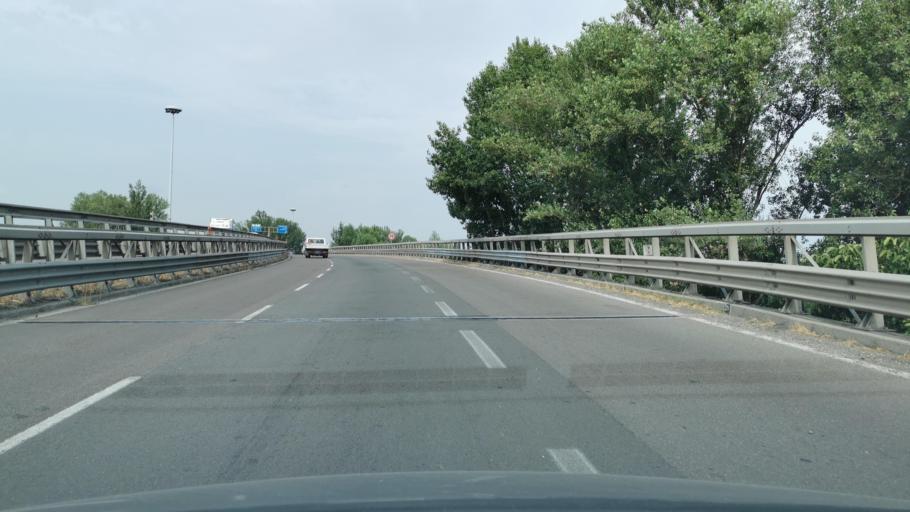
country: IT
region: Emilia-Romagna
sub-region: Provincia di Modena
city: Villanova
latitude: 44.6722
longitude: 10.9133
